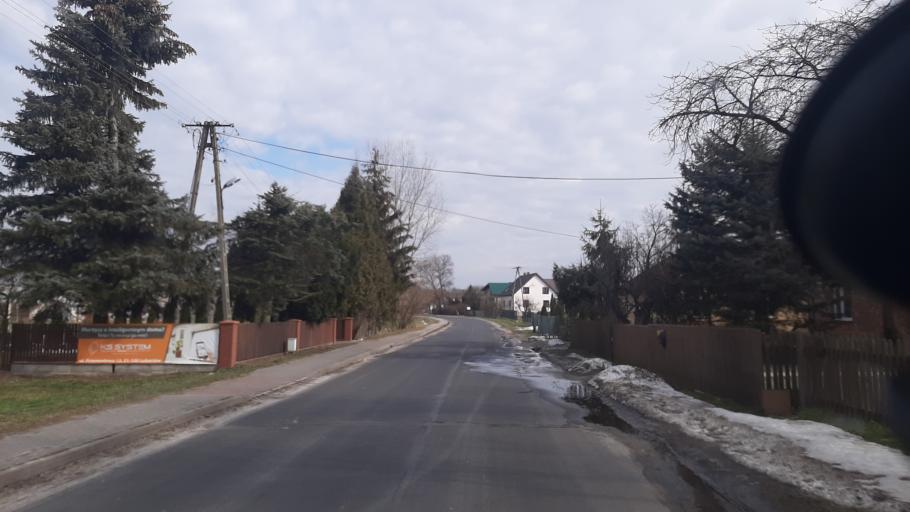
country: PL
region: Lublin Voivodeship
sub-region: Powiat lubartowski
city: Wola Sernicka
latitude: 51.4672
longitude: 22.7376
